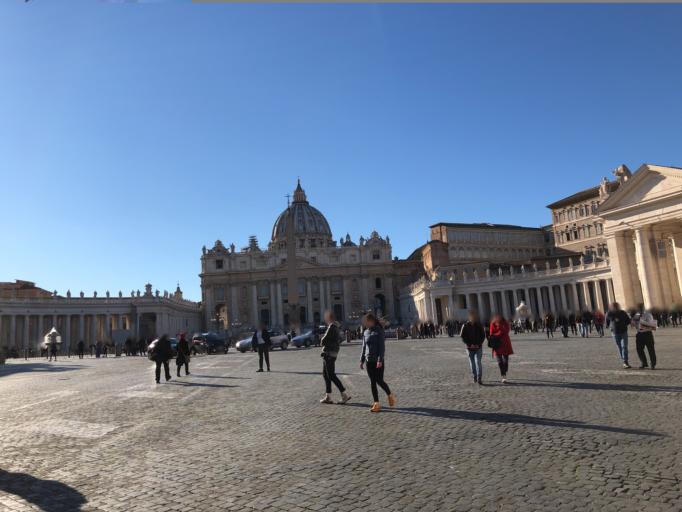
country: VA
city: Vatican City
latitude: 41.9023
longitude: 12.4590
